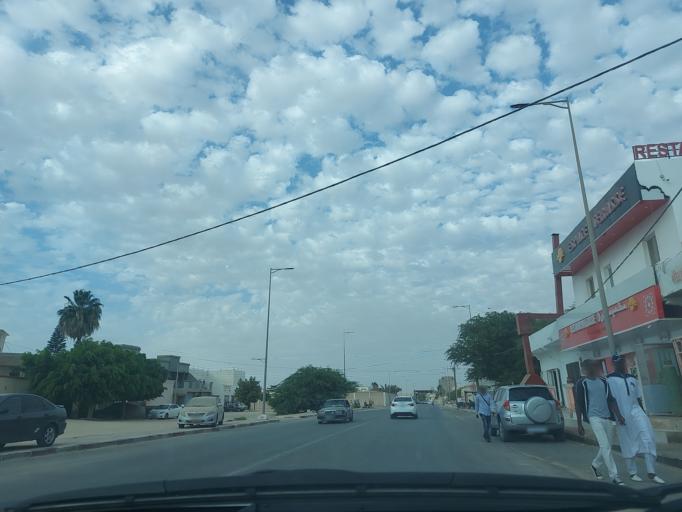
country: MR
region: Nouakchott
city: Nouakchott
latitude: 18.1089
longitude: -15.9963
